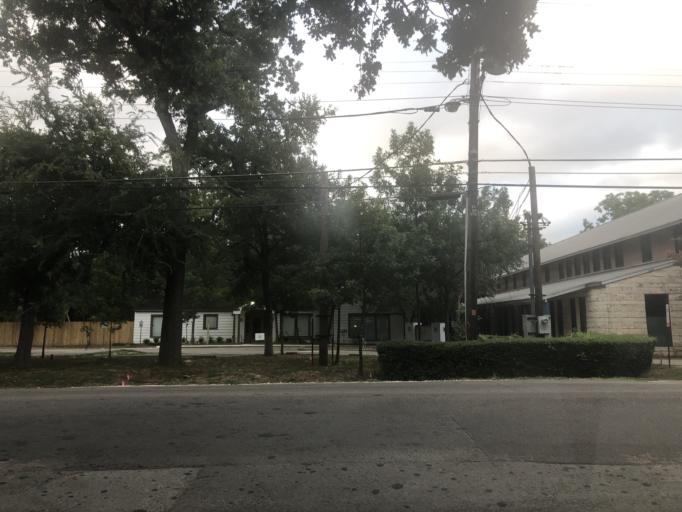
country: US
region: Texas
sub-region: Dallas County
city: University Park
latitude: 32.8307
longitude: -96.8494
